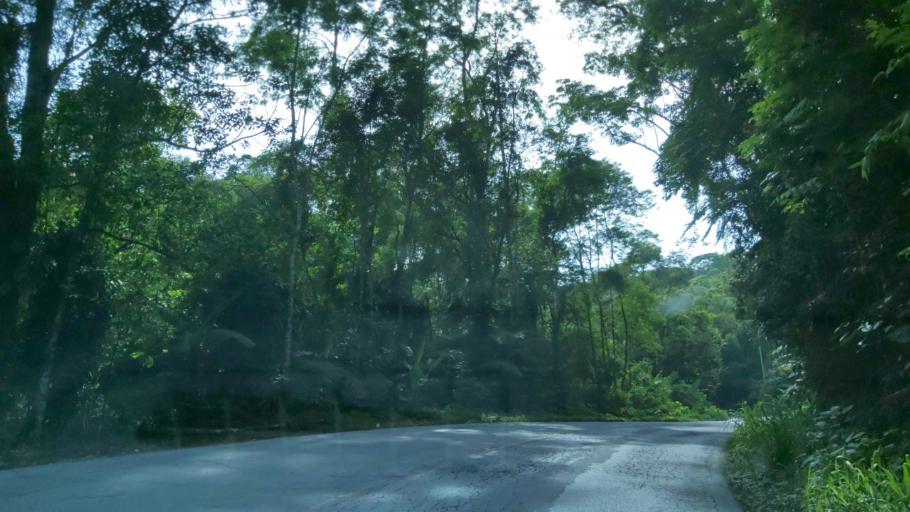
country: BR
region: Sao Paulo
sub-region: Miracatu
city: Miracatu
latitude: -24.0542
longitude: -47.5828
